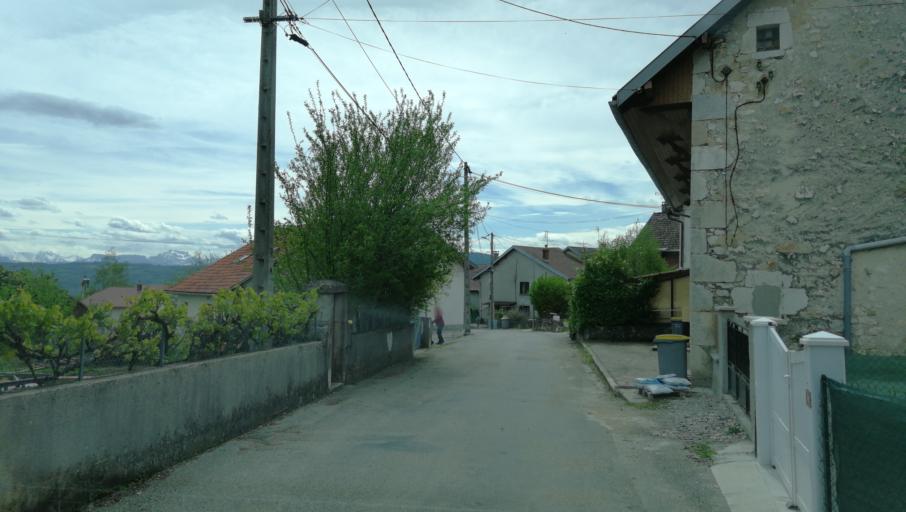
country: FR
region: Rhone-Alpes
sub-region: Departement de l'Ain
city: Bellegarde-sur-Valserine
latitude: 46.0069
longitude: 5.7844
